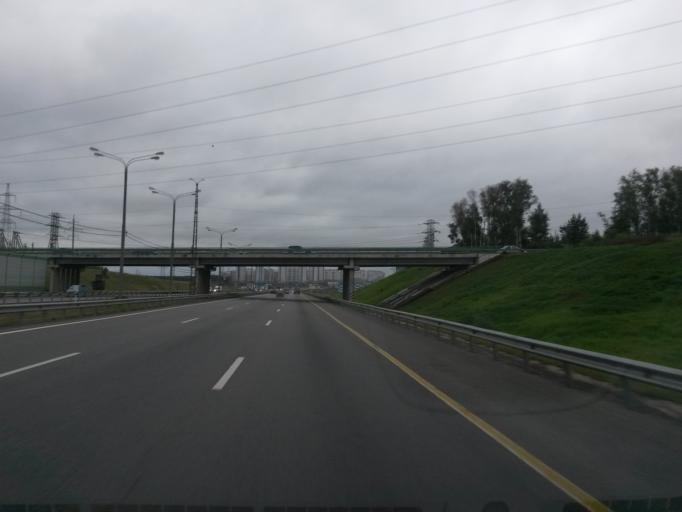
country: RU
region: Moskovskaya
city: Vostryakovo
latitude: 55.3773
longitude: 37.7795
